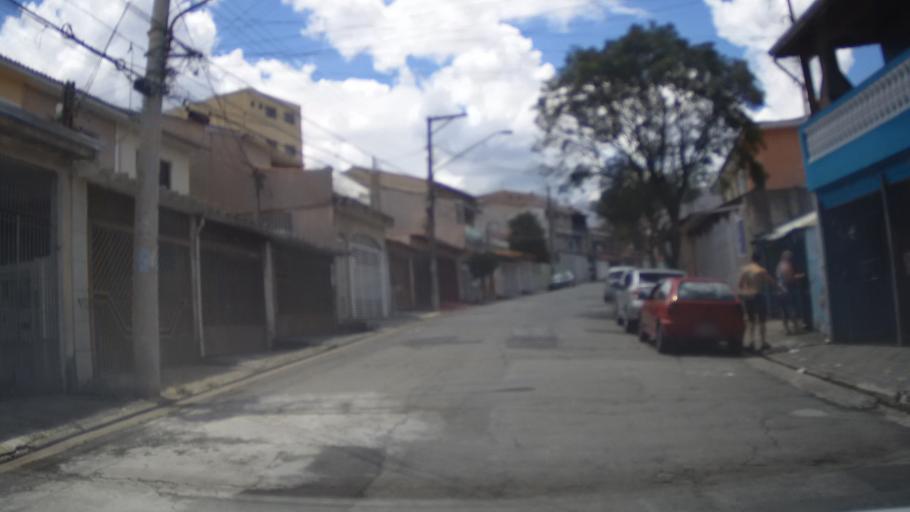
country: BR
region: Sao Paulo
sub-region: Guarulhos
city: Guarulhos
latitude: -23.4522
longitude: -46.5410
